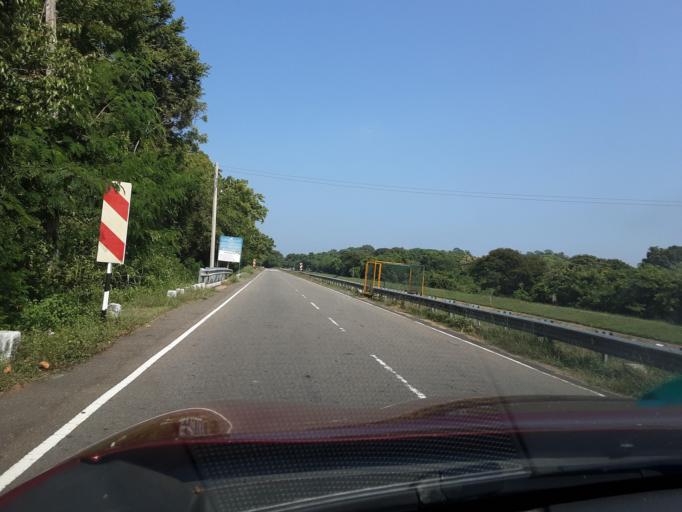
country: LK
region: Uva
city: Badulla
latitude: 7.2789
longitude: 81.0444
